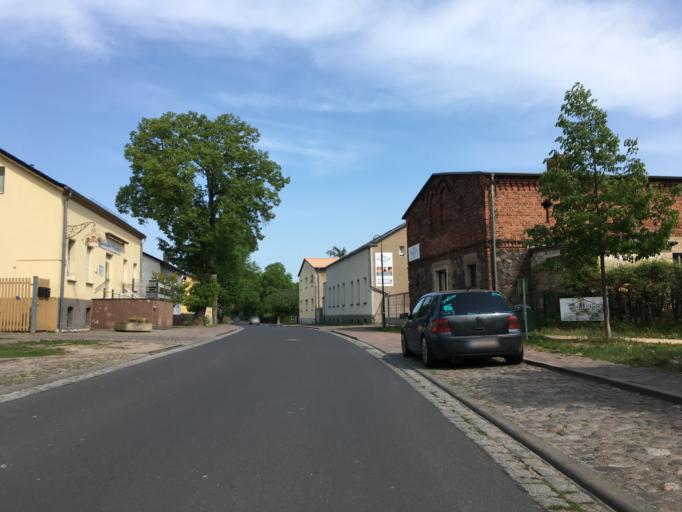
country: DE
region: Brandenburg
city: Werneuchen
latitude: 52.6015
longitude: 13.7565
